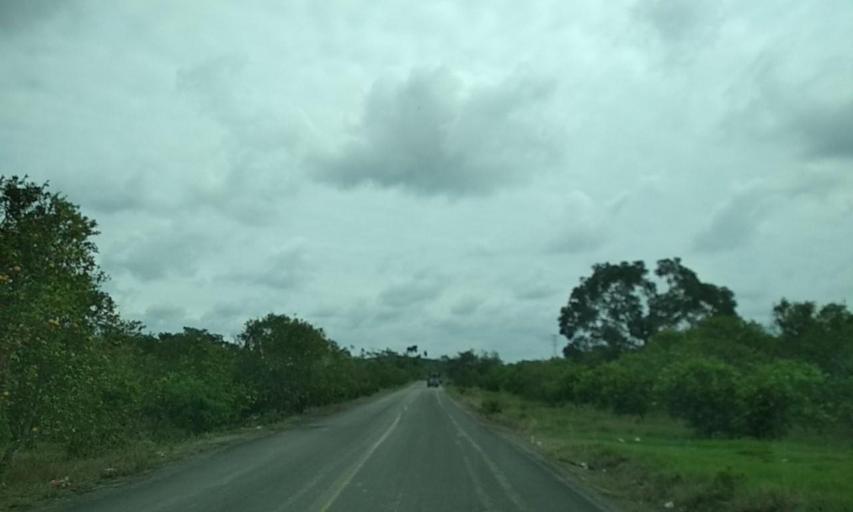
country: MX
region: Veracruz
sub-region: Papantla
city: El Chote
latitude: 20.3531
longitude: -97.3575
